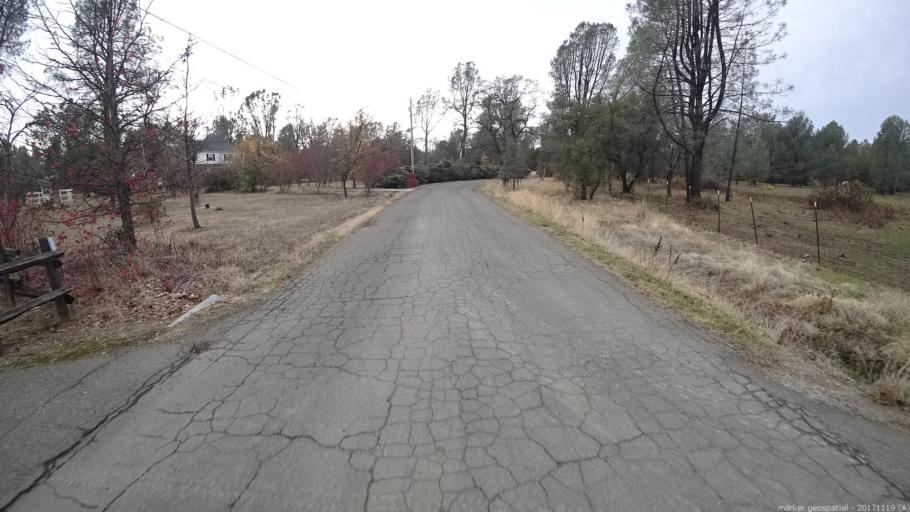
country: US
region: California
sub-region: Shasta County
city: Shasta
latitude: 40.4790
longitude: -122.4606
